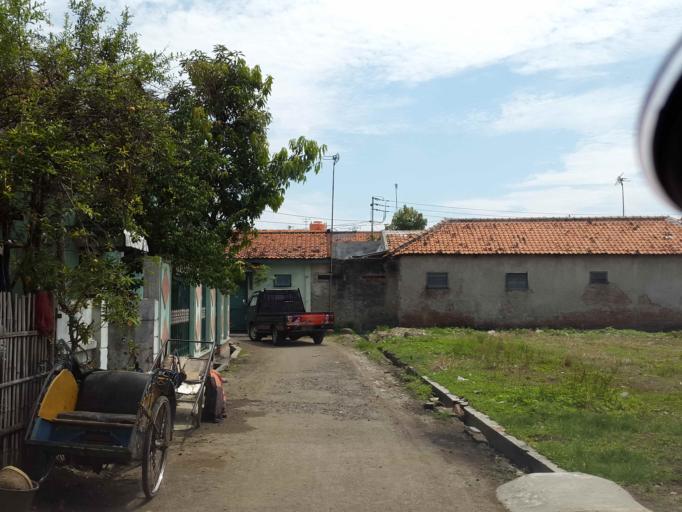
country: ID
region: Central Java
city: Dukuhturi
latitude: -6.8747
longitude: 109.0613
